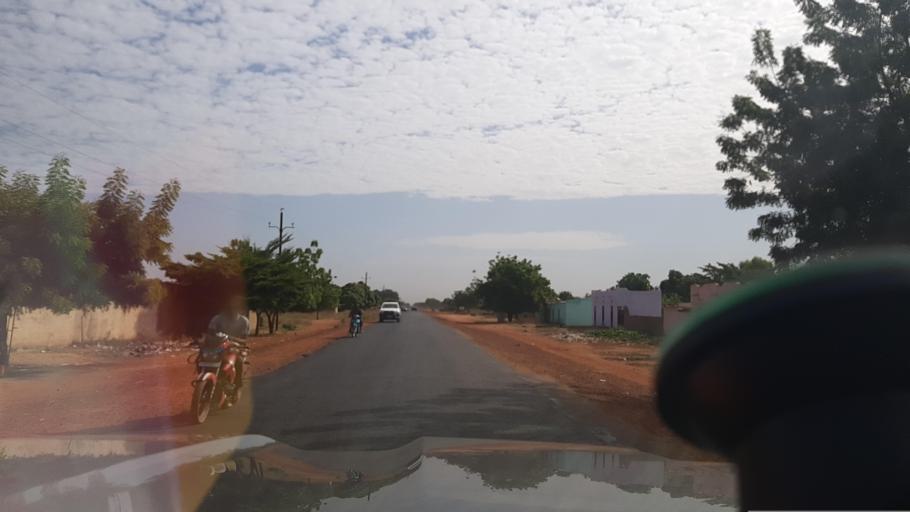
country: ML
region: Segou
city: Segou
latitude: 13.4959
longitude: -6.1681
